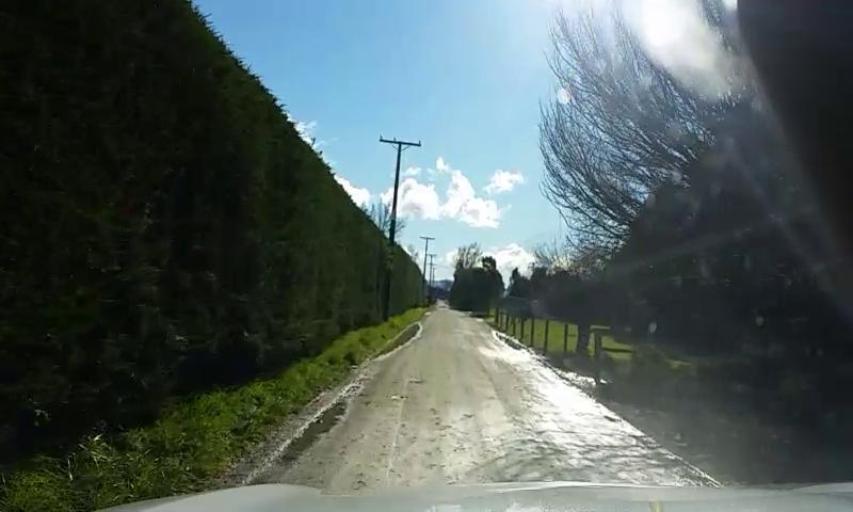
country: NZ
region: Tasman
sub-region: Tasman District
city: Richmond
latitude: -41.3026
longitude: 173.1442
